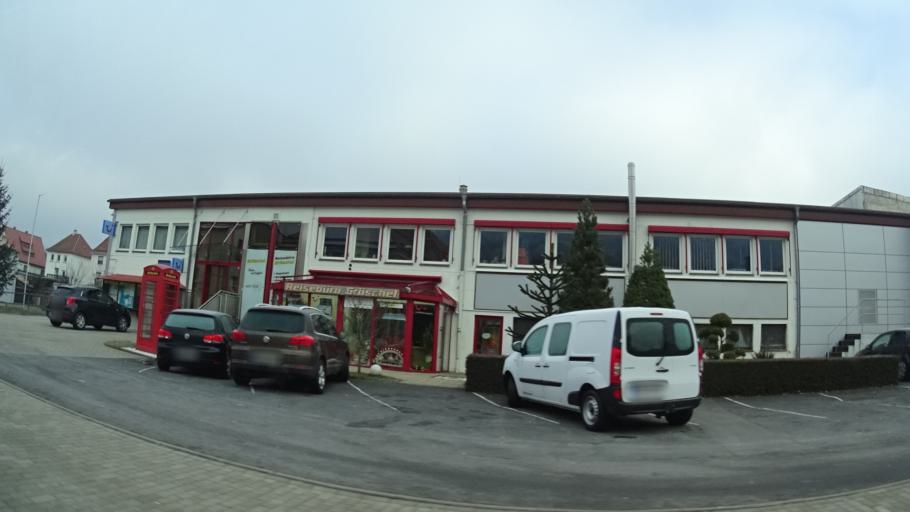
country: DE
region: Thuringia
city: Zella-Mehlis
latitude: 50.6559
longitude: 10.6596
